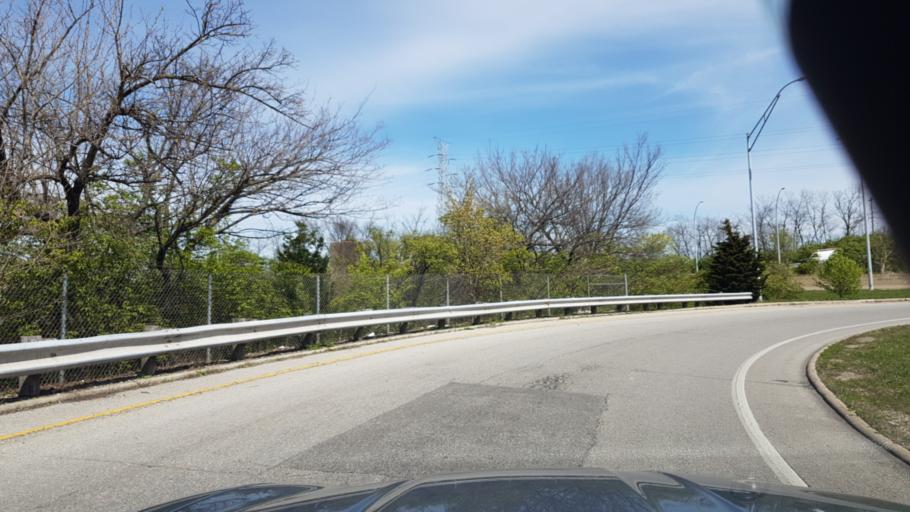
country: US
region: Kentucky
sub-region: Kenton County
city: Ludlow
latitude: 39.0998
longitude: -84.5344
